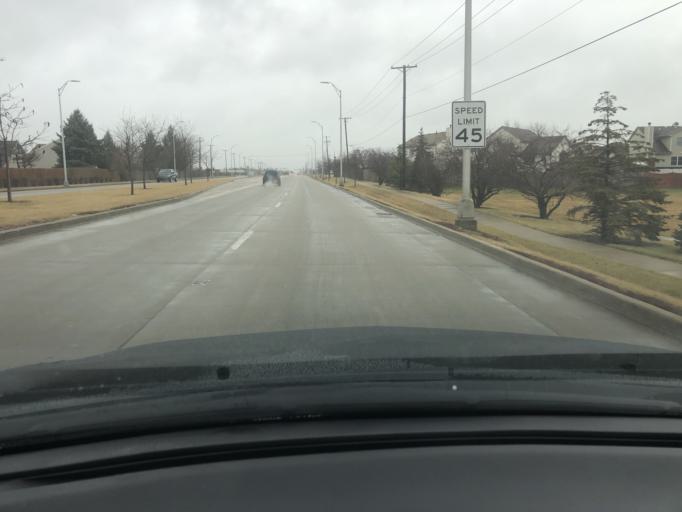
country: US
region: Illinois
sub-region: Will County
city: Shorewood
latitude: 41.5557
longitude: -88.2001
